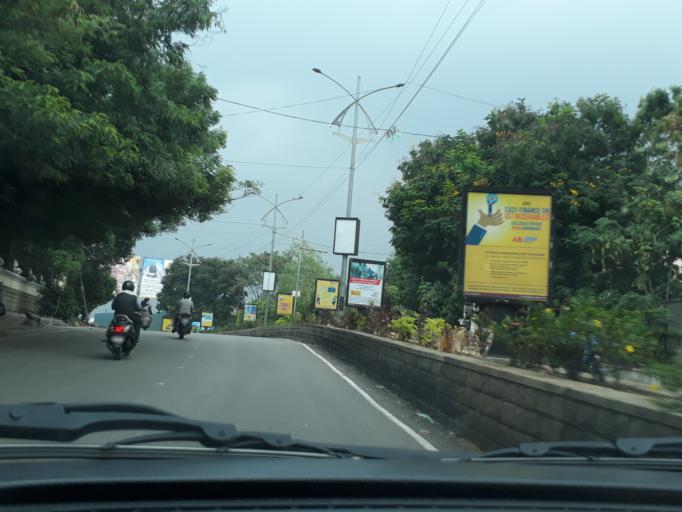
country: IN
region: Telangana
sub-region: Rangareddi
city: Kukatpalli
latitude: 17.4321
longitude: 78.4186
